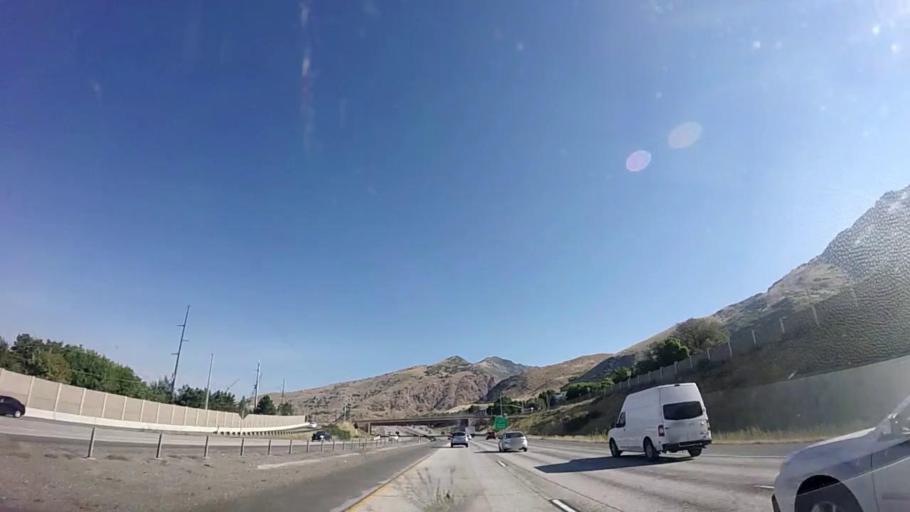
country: US
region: Utah
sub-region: Salt Lake County
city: Mount Olympus
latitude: 40.6977
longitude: -111.7955
